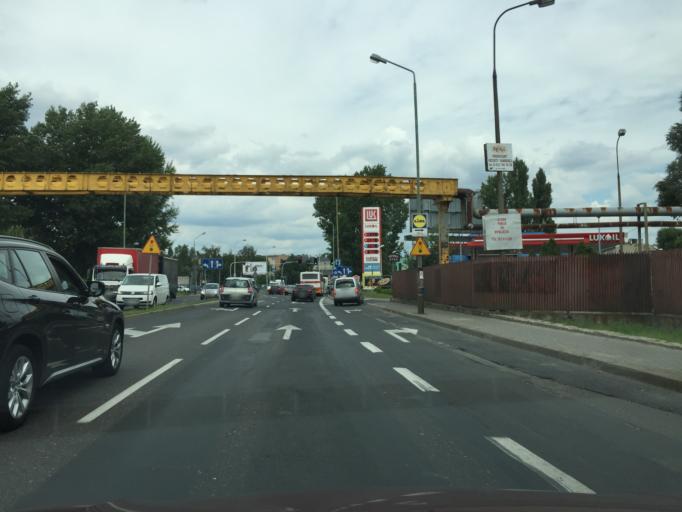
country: PL
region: Greater Poland Voivodeship
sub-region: Kalisz
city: Kalisz
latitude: 51.7642
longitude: 18.0791
